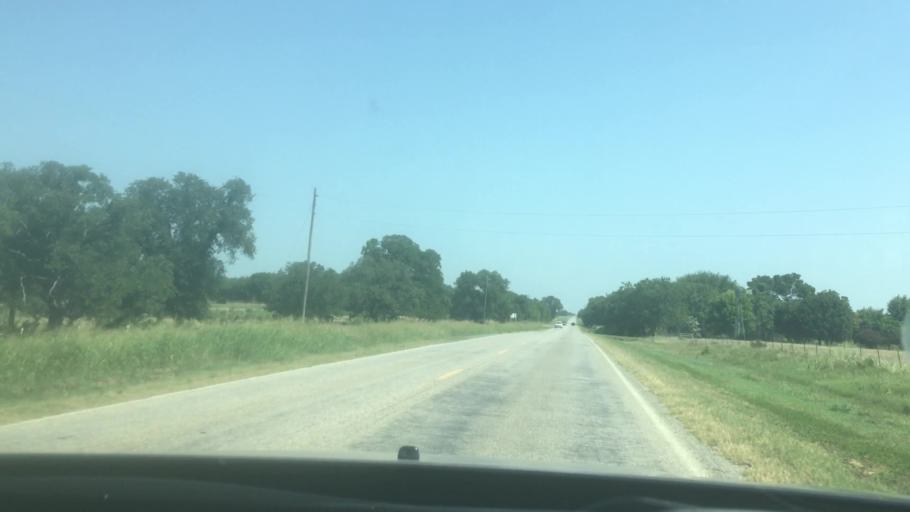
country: US
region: Oklahoma
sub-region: Johnston County
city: Tishomingo
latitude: 34.2918
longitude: -96.4248
